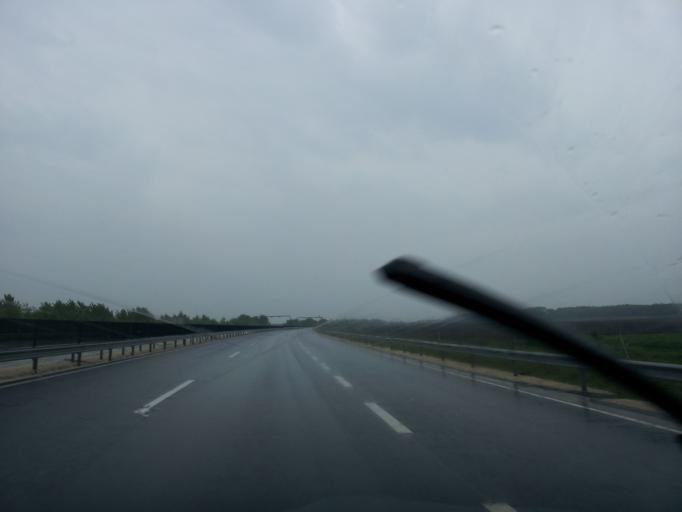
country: HU
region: Tolna
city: Szedres
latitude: 46.4428
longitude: 18.7077
